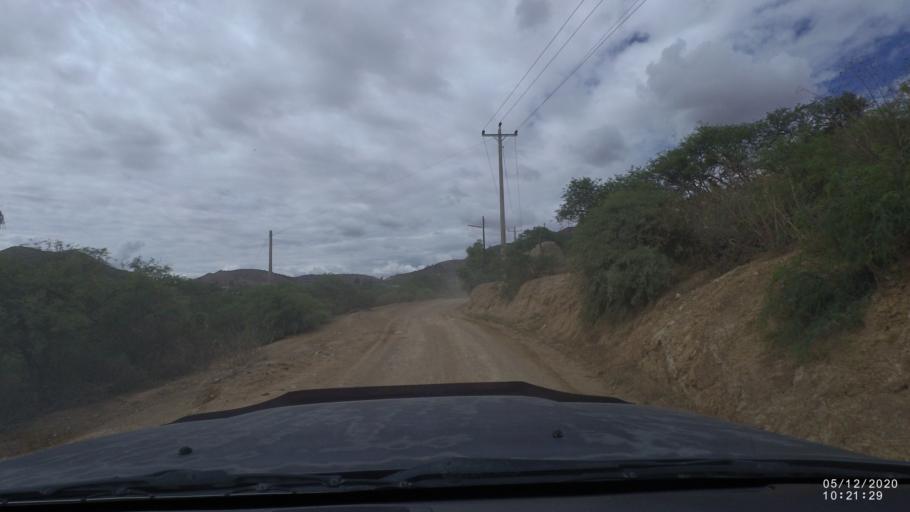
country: BO
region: Cochabamba
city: Sipe Sipe
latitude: -17.4903
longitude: -66.2820
